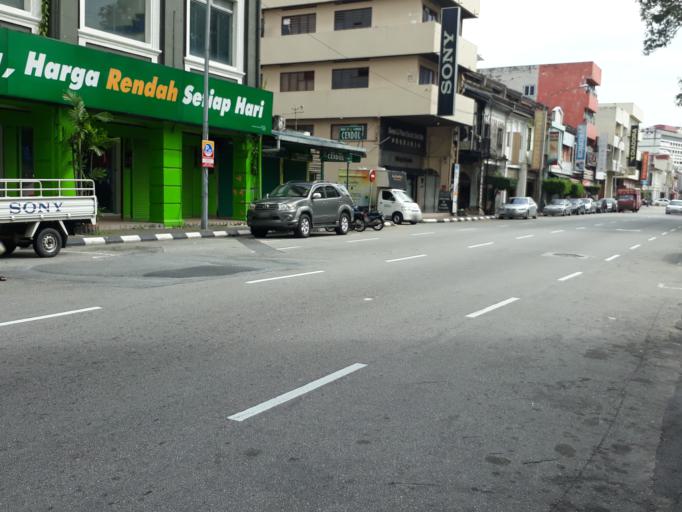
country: MY
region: Perak
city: Ipoh
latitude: 4.5954
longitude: 101.0838
